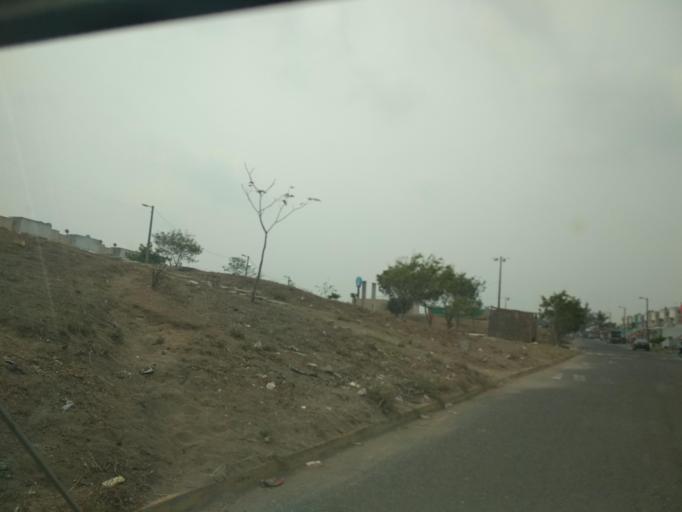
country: MX
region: Veracruz
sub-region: Veracruz
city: Fraccionamiento Geovillas los Pinos
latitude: 19.2258
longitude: -96.2442
